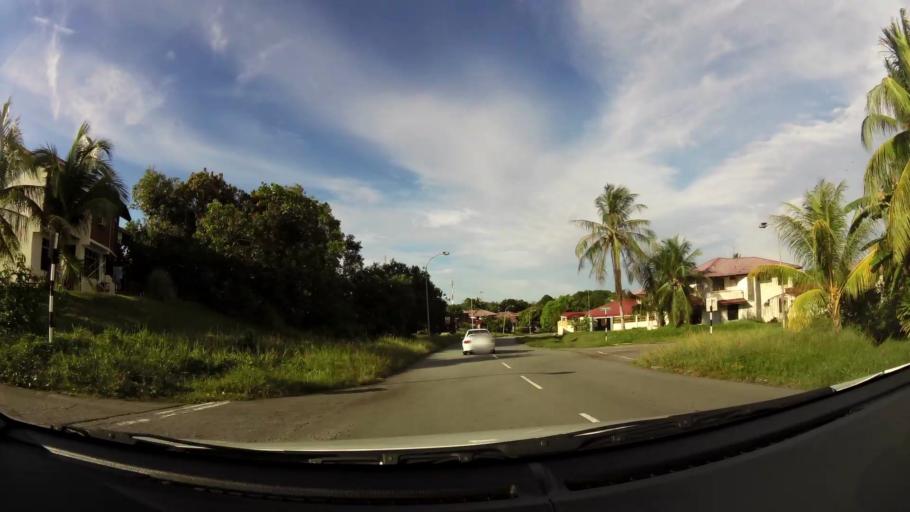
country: BN
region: Brunei and Muara
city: Bandar Seri Begawan
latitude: 4.9882
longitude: 114.9702
